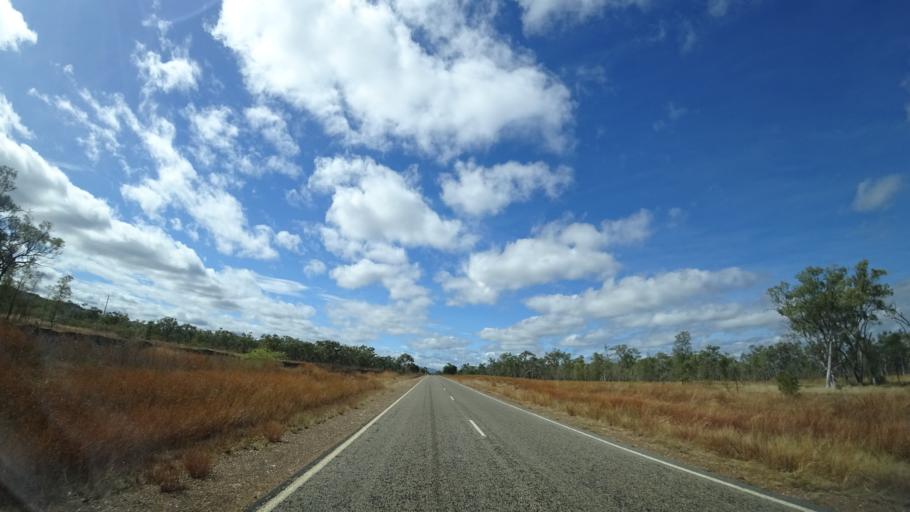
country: AU
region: Queensland
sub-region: Cairns
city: Port Douglas
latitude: -16.4901
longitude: 144.9270
